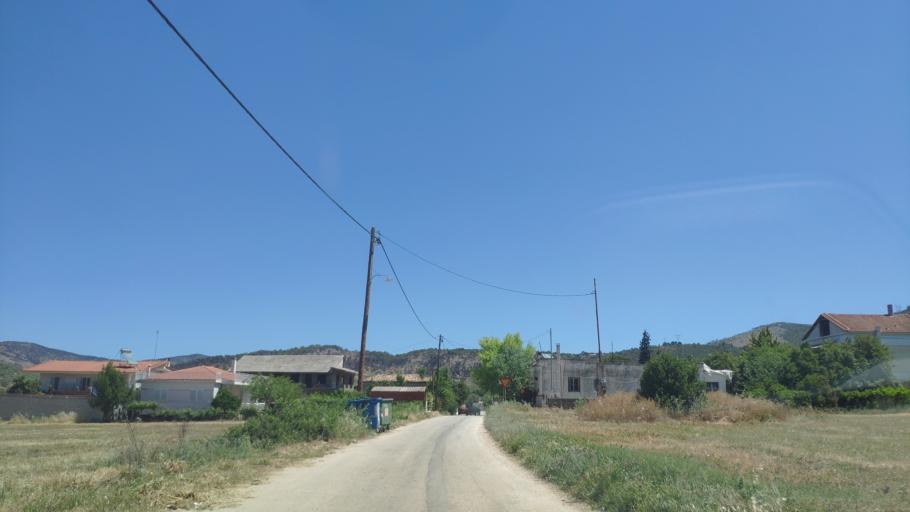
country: GR
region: Peloponnese
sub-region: Nomos Korinthias
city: Athikia
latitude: 37.8215
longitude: 22.9247
